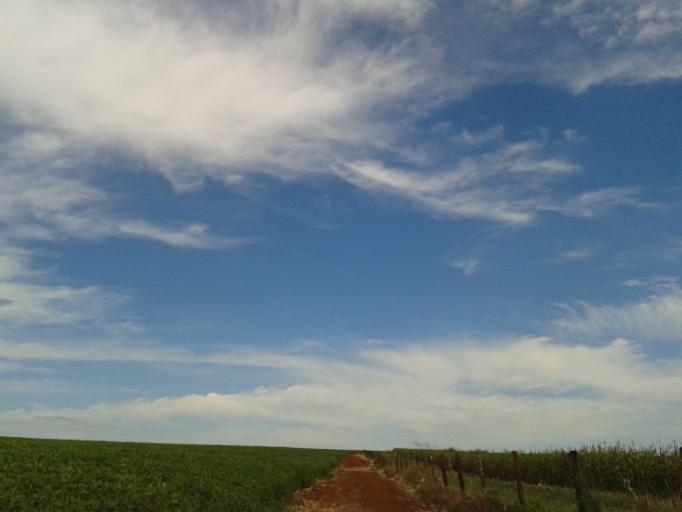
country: BR
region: Minas Gerais
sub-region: Capinopolis
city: Capinopolis
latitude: -18.6527
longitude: -49.7120
